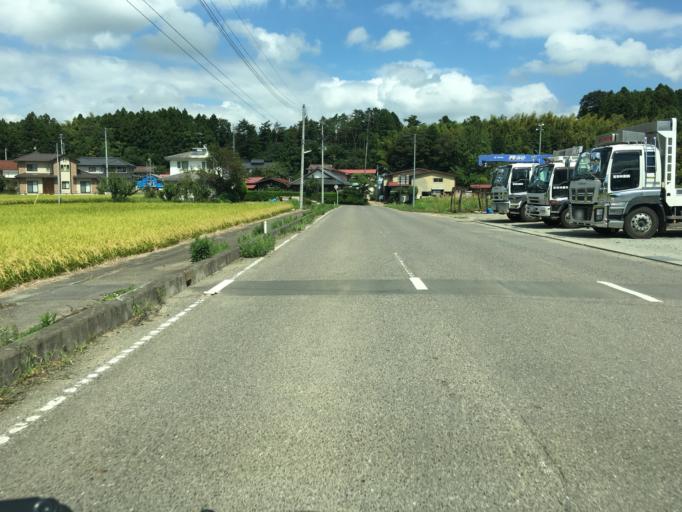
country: JP
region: Fukushima
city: Motomiya
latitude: 37.5521
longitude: 140.3766
